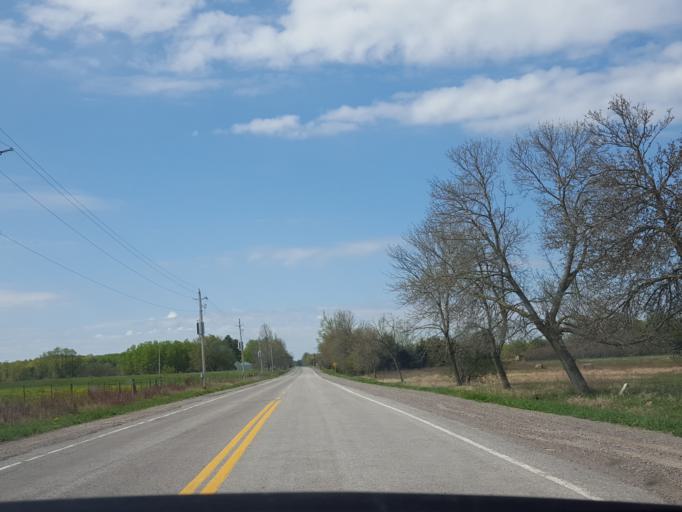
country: CA
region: Ontario
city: Uxbridge
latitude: 44.2003
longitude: -78.8765
